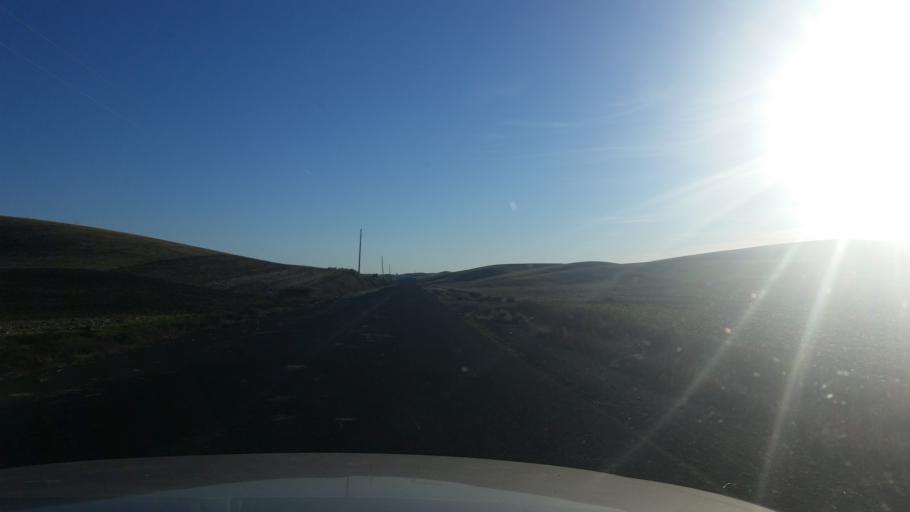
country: US
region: Washington
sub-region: Spokane County
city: Cheney
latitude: 47.3604
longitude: -117.4473
